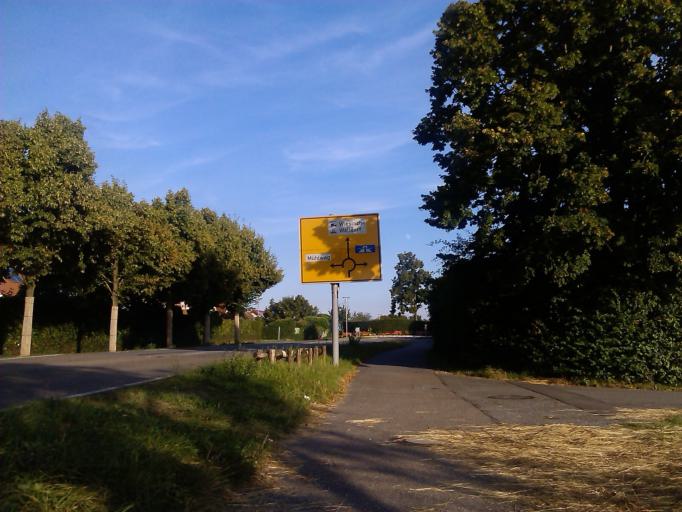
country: DE
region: Baden-Wuerttemberg
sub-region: Karlsruhe Region
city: Walldorf
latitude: 49.2984
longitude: 8.6497
